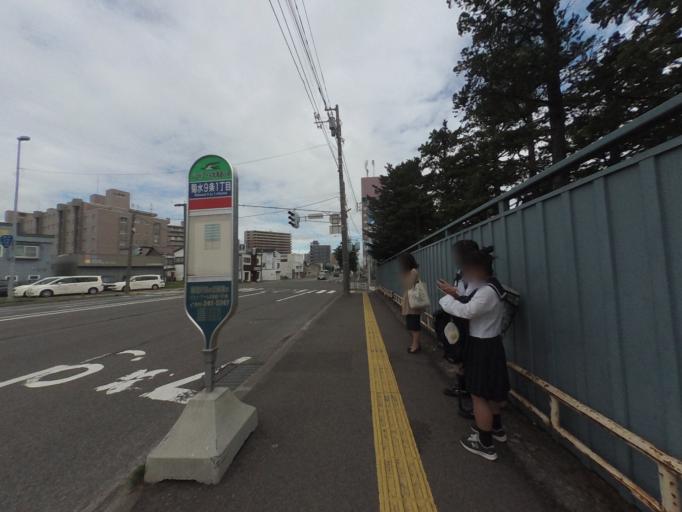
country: JP
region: Hokkaido
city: Sapporo
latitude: 43.0641
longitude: 141.3809
